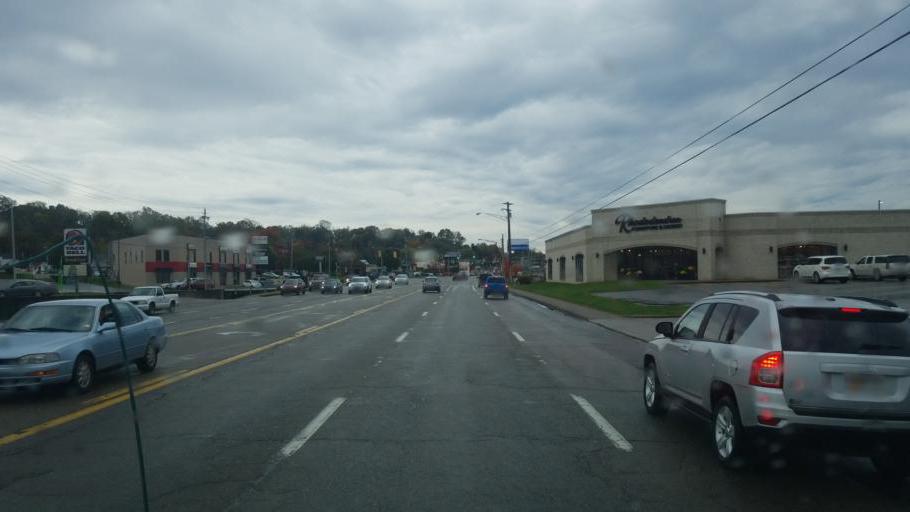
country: US
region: West Virginia
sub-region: Wood County
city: Vienna
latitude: 39.3047
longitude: -81.5504
